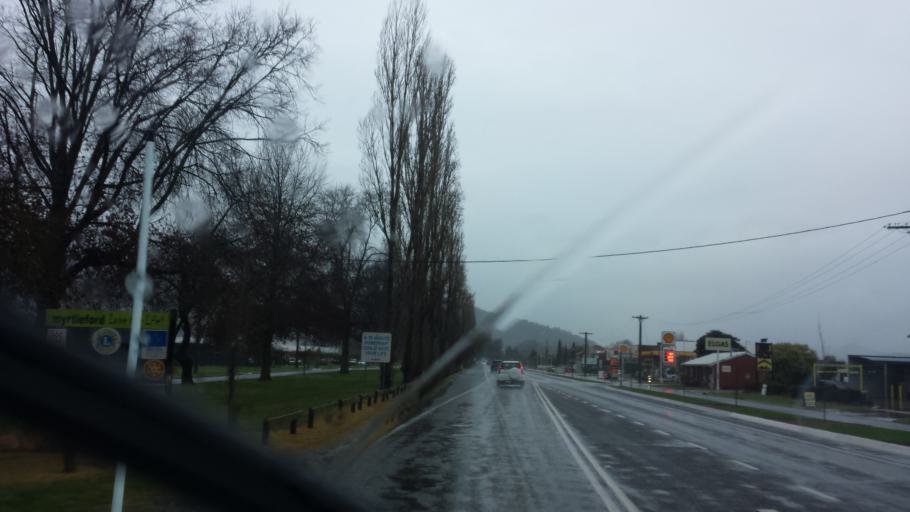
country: AU
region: Victoria
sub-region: Wangaratta
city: Wangaratta
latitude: -36.5554
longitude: 146.7150
